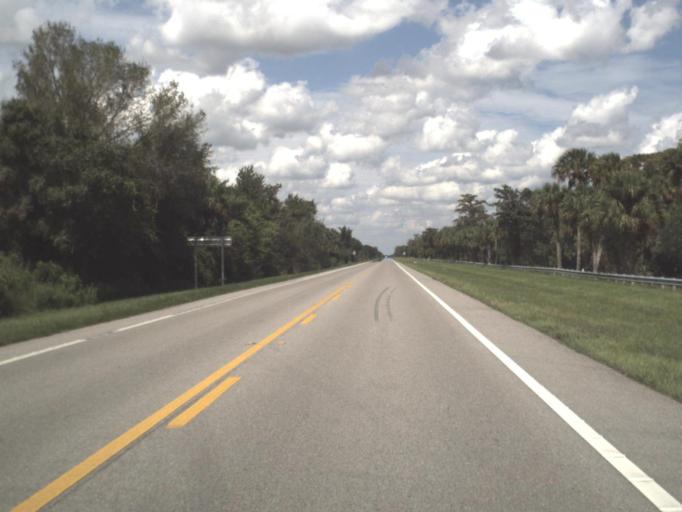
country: US
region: Florida
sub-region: Collier County
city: Immokalee
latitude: 26.3046
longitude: -81.3427
